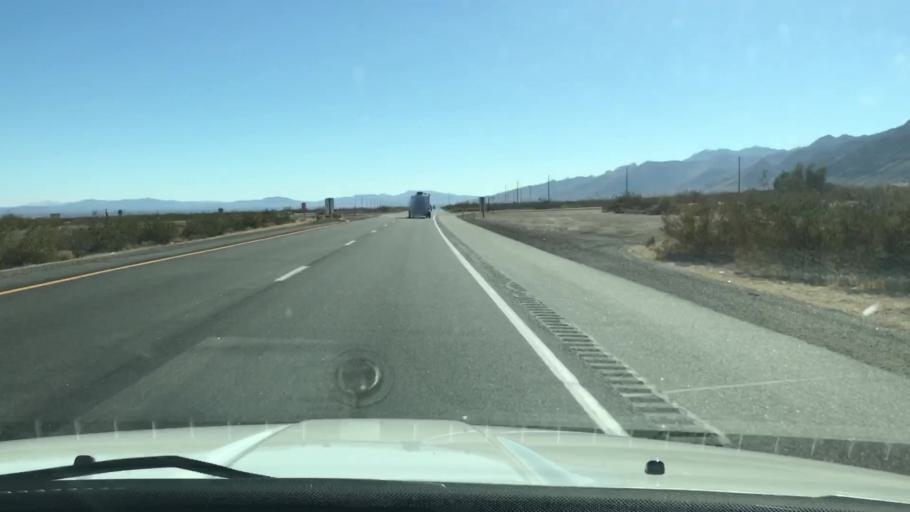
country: US
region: California
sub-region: Kern County
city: Inyokern
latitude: 35.8434
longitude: -117.8753
